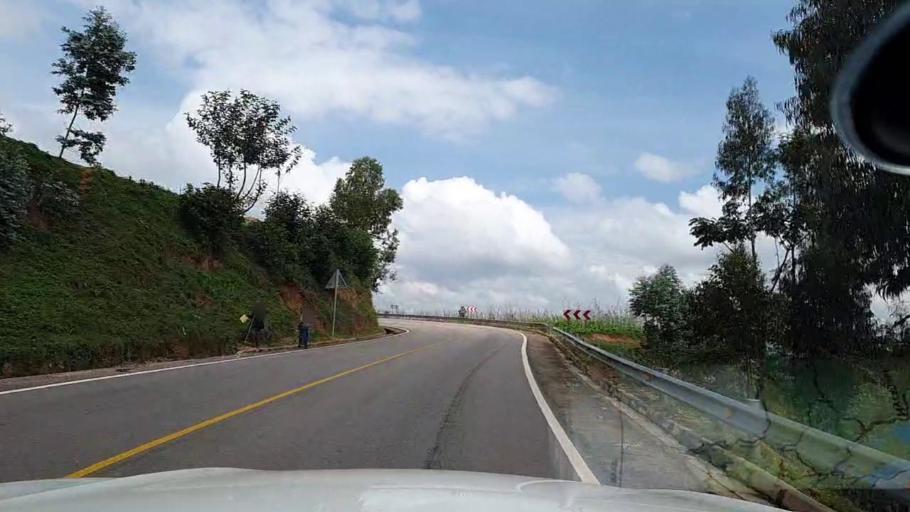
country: RW
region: Southern Province
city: Nzega
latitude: -2.5046
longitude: 29.5015
